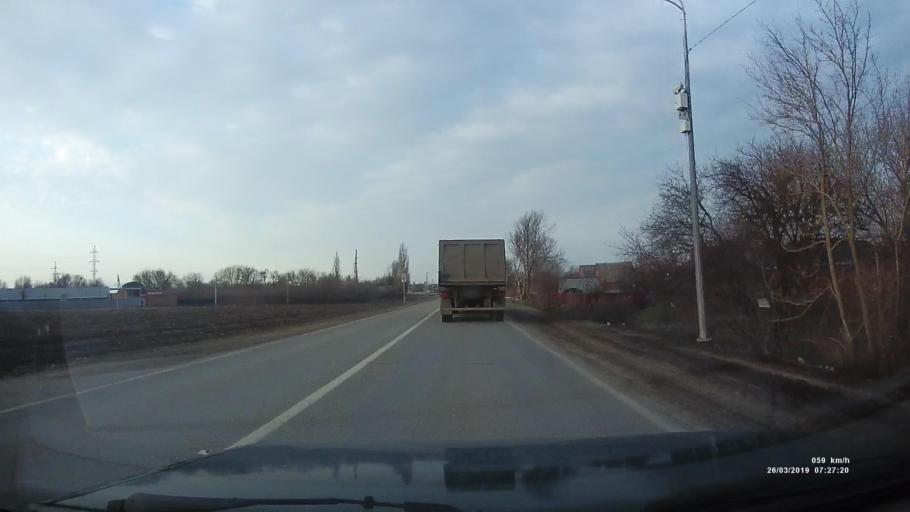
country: RU
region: Rostov
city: Taganrog
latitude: 47.2630
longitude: 38.8292
